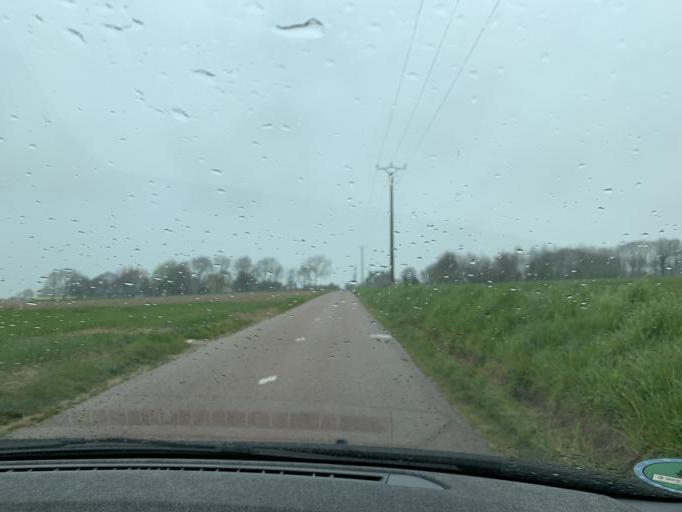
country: FR
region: Haute-Normandie
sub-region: Departement de la Seine-Maritime
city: Les Loges
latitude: 49.7195
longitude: 0.2783
